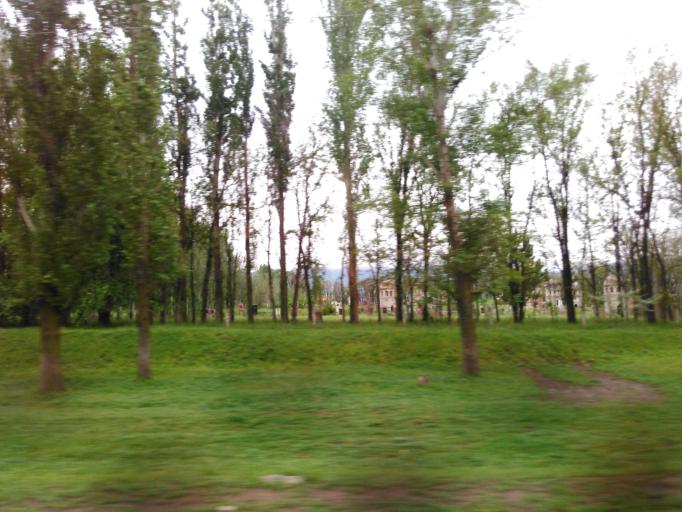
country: KG
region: Chuy
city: Chuy
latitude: 42.7473
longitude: 75.2703
